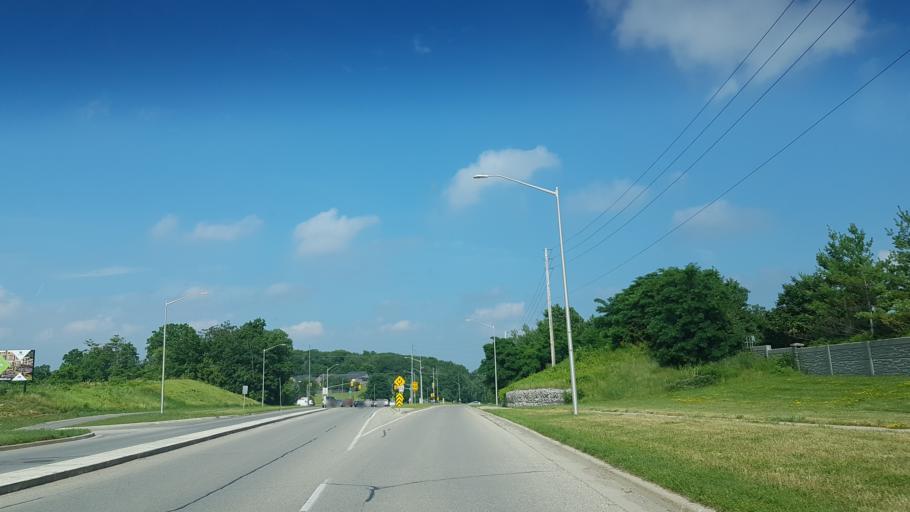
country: CA
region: Ontario
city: Delaware
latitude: 42.9663
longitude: -81.3571
